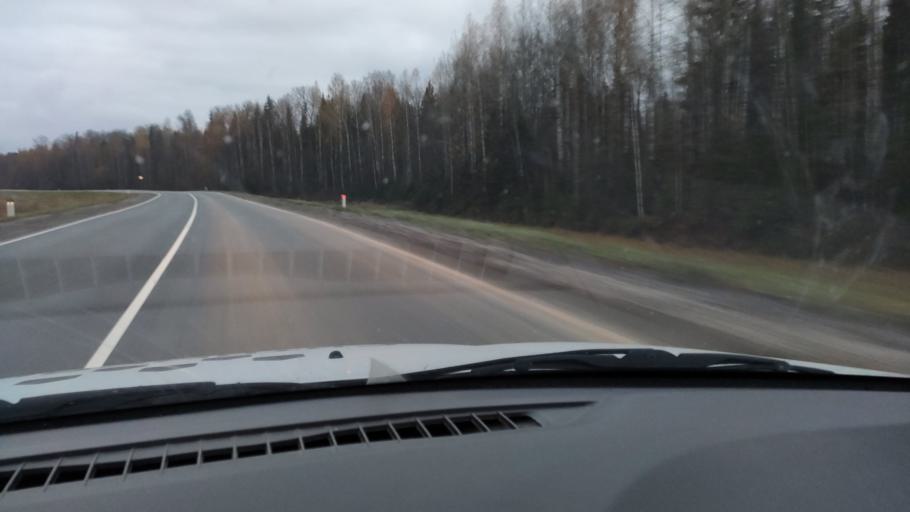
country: RU
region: Kirov
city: Kostino
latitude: 58.8405
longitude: 53.0721
